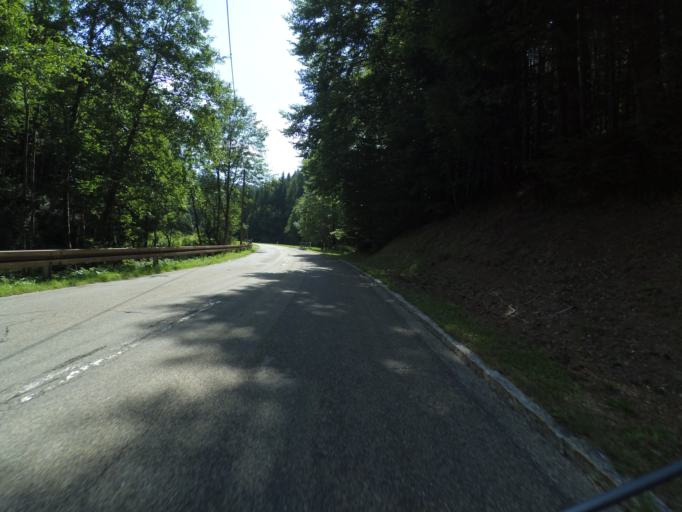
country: DE
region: Baden-Wuerttemberg
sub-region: Freiburg Region
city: Sankt Peter
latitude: 48.0424
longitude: 8.0434
